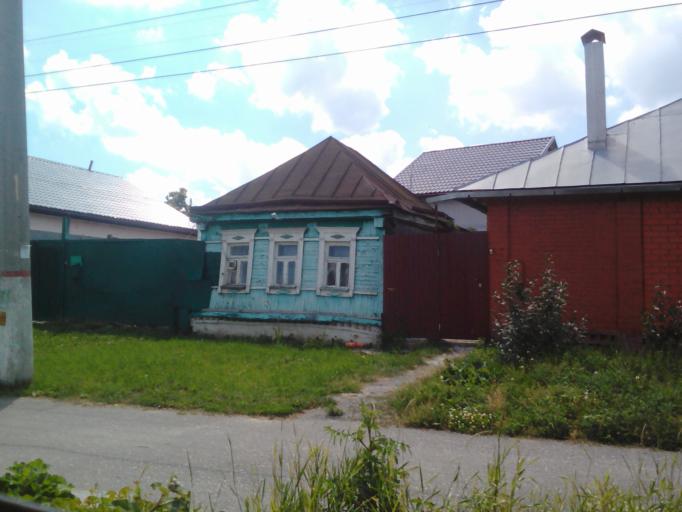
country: RU
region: Kursk
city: Kursk
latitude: 51.7406
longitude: 36.1723
